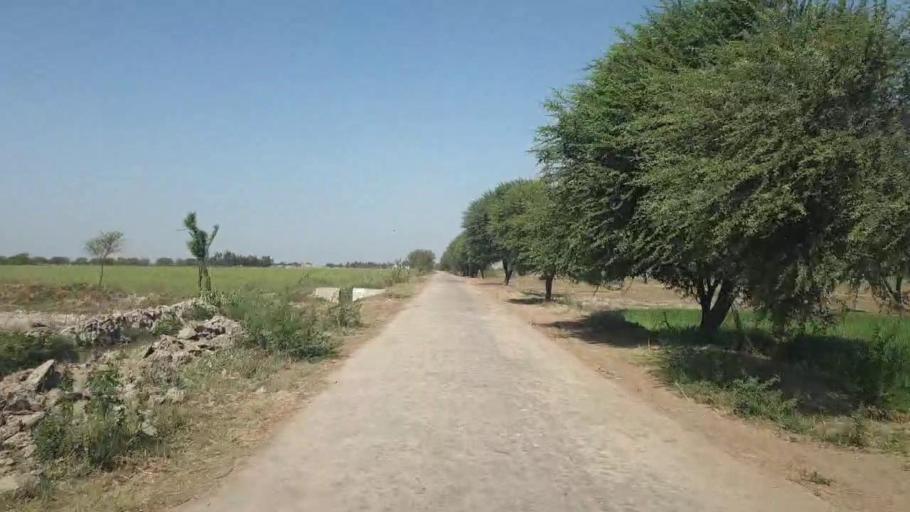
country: PK
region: Sindh
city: Umarkot
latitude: 25.2929
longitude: 69.6333
